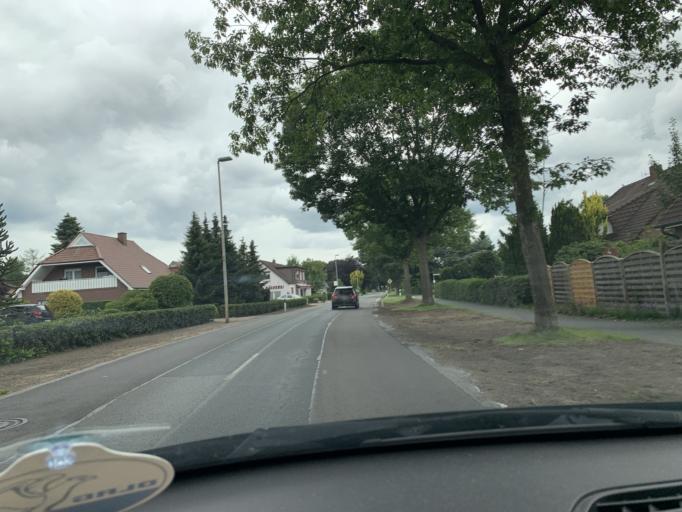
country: DE
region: Lower Saxony
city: Edewecht
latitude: 53.1226
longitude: 7.9263
